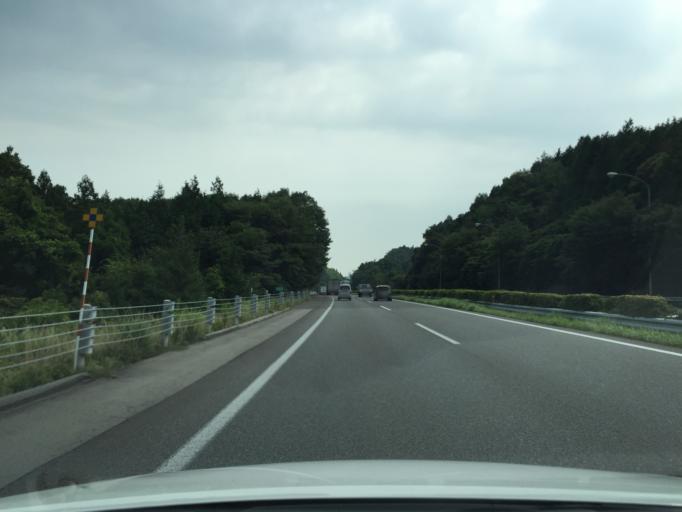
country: JP
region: Fukushima
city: Iwaki
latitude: 37.0186
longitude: 140.8133
